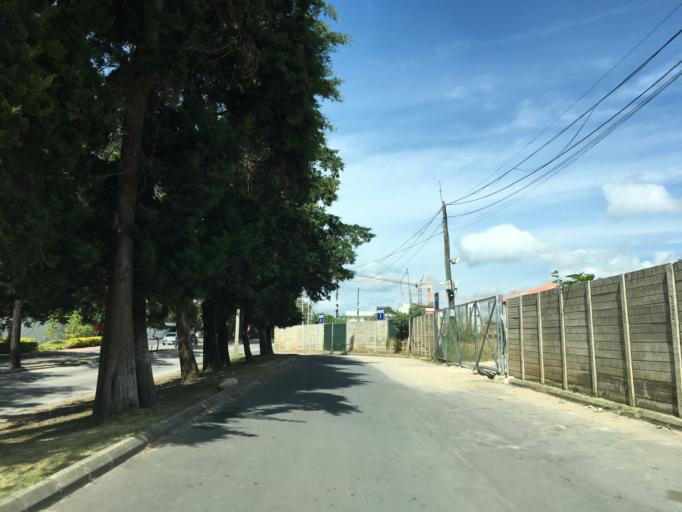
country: GT
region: Guatemala
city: Guatemala City
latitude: 14.6154
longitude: -90.4838
